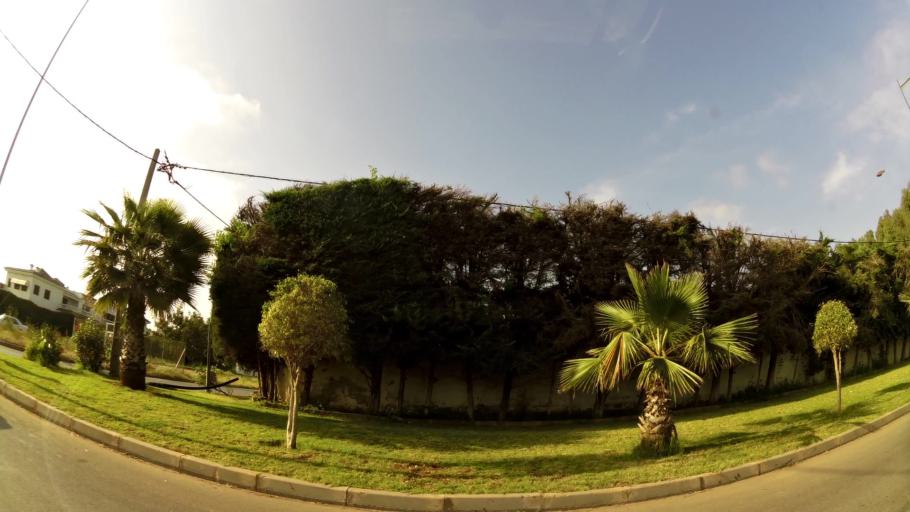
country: MA
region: Rabat-Sale-Zemmour-Zaer
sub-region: Rabat
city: Rabat
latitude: 33.9336
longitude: -6.8118
